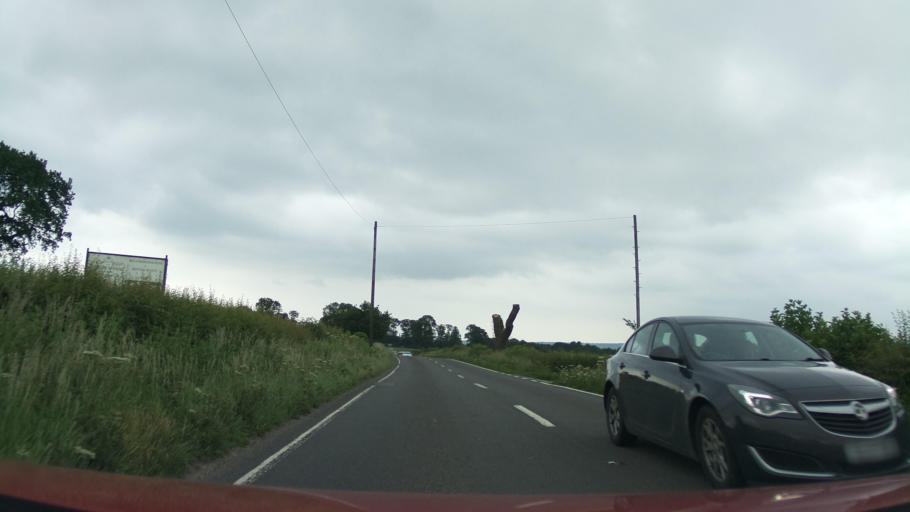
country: GB
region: England
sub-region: Derbyshire
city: Rodsley
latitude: 52.9163
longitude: -1.7605
